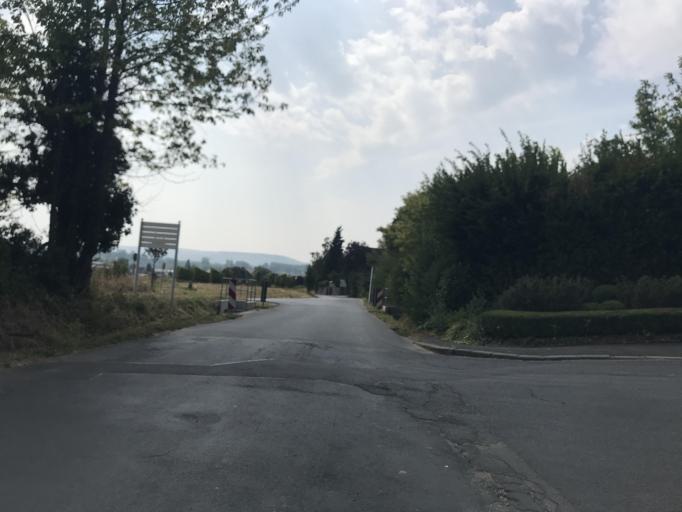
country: DE
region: Rheinland-Pfalz
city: Oestrich-Winkel
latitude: 50.0126
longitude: 8.0339
